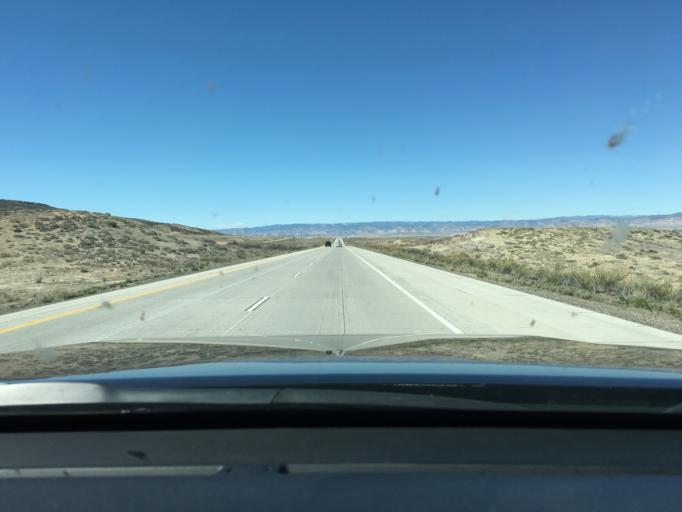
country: US
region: Colorado
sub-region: Mesa County
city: Loma
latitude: 39.1951
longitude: -108.8436
